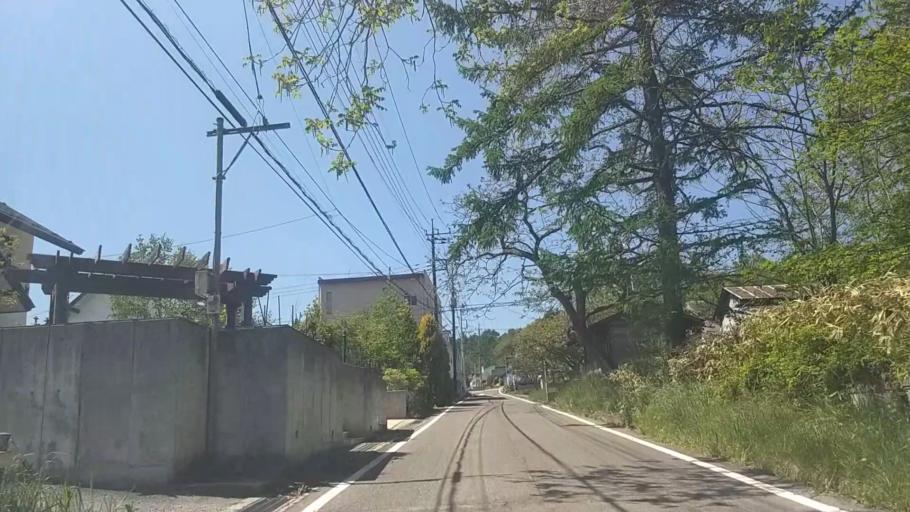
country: JP
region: Yamanashi
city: Nirasaki
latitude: 35.9063
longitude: 138.4452
